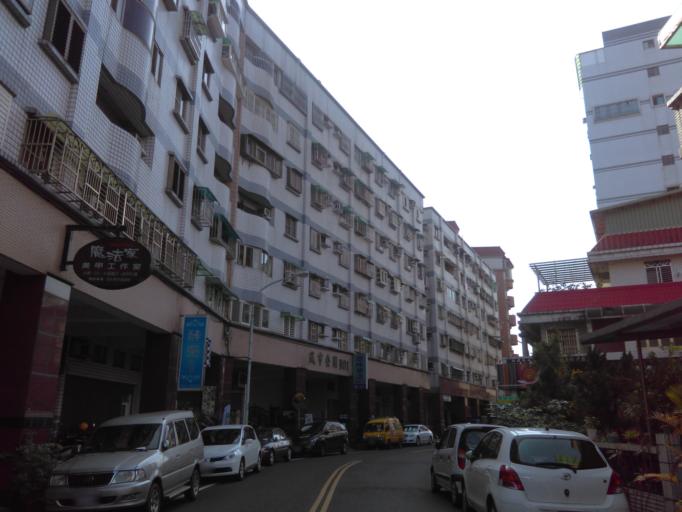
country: TW
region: Taiwan
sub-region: Yilan
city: Yilan
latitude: 24.7429
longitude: 121.7508
